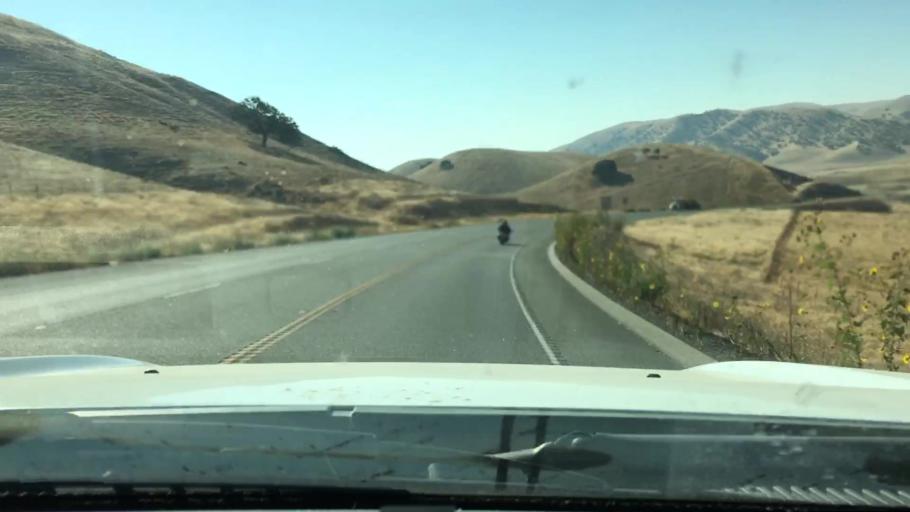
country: US
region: California
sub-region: San Luis Obispo County
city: Shandon
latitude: 35.7425
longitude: -120.2142
